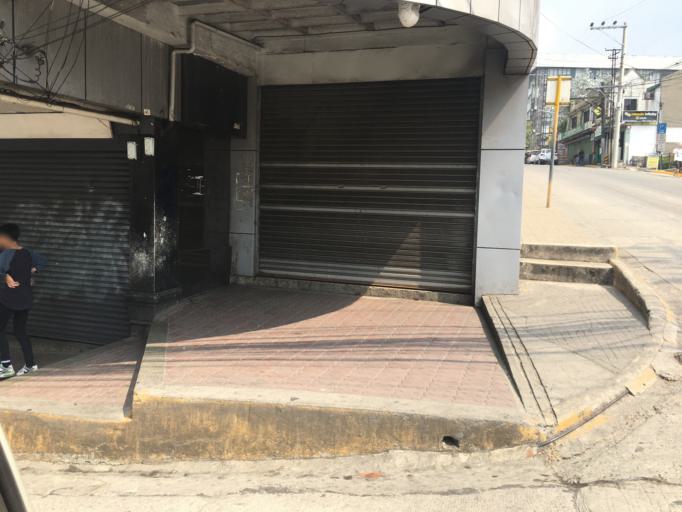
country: PH
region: Cordillera
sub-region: Baguio City
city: Baguio
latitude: 16.4145
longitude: 120.5976
